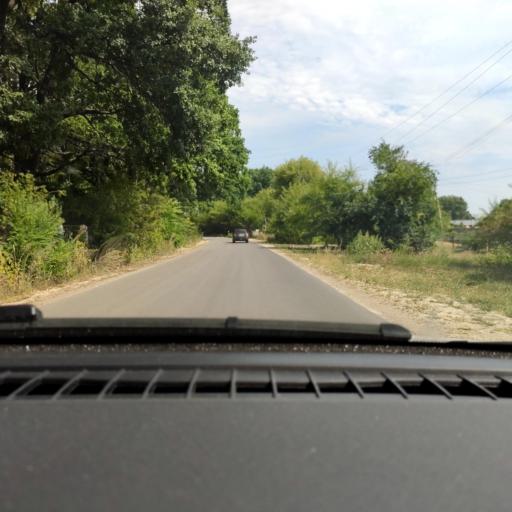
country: RU
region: Voronezj
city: Pridonskoy
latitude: 51.7398
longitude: 39.0693
